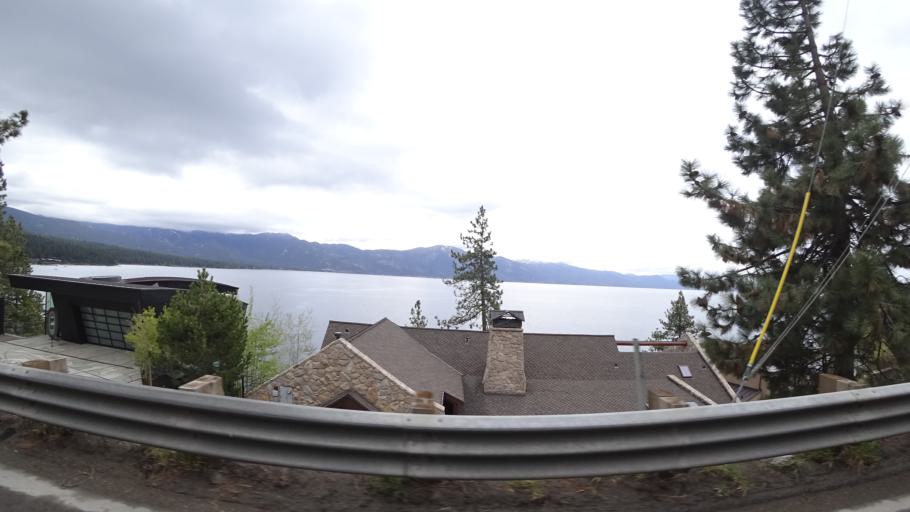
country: US
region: Nevada
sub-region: Washoe County
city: Incline Village
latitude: 39.2434
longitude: -119.9991
